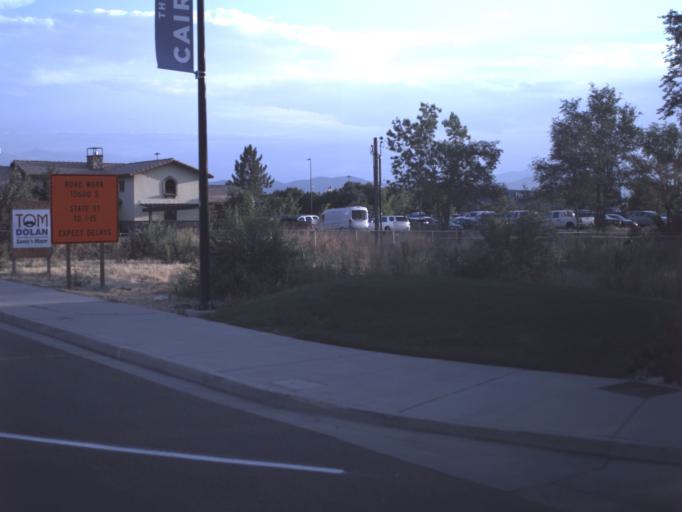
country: US
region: Utah
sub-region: Salt Lake County
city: White City
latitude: 40.5607
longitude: -111.8910
